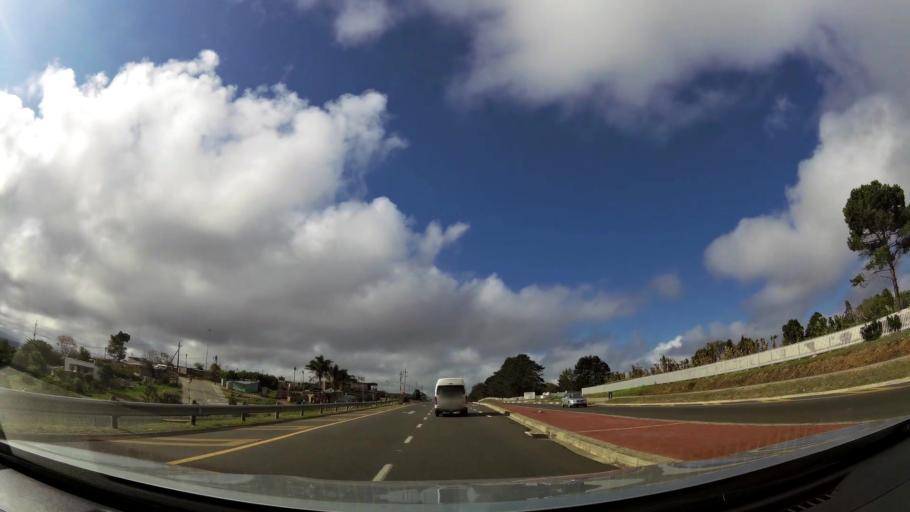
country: ZA
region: Western Cape
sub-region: Eden District Municipality
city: Plettenberg Bay
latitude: -34.0536
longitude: 23.3474
